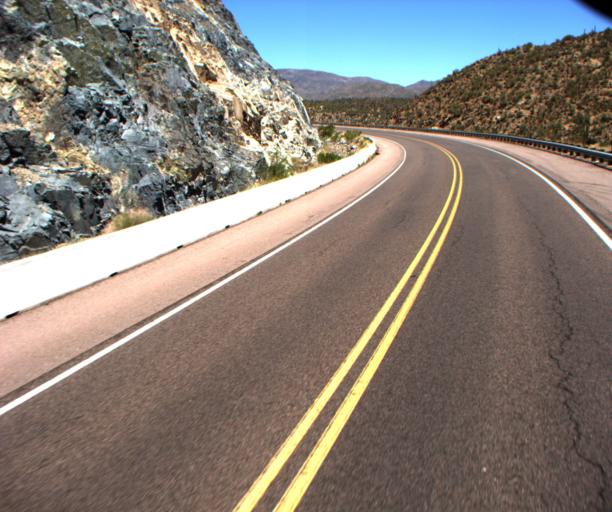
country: US
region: Arizona
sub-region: Pinal County
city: Kearny
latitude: 33.0721
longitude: -110.7234
